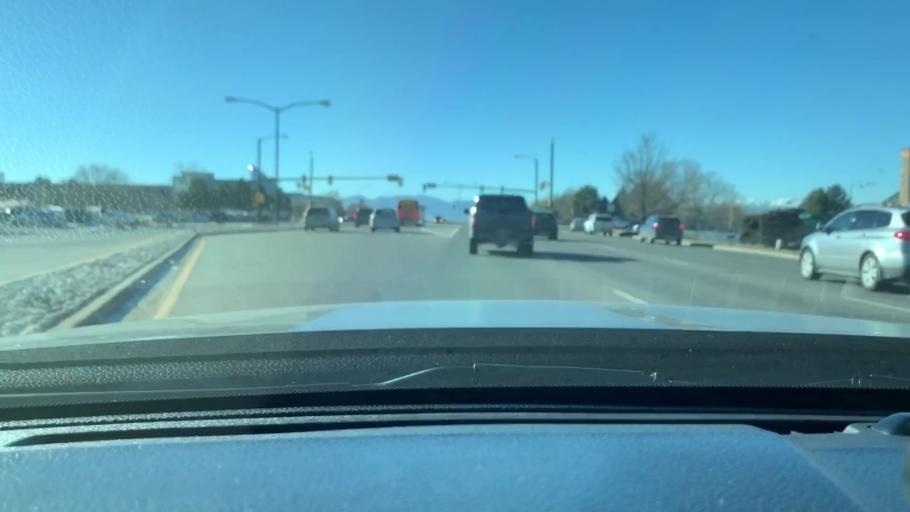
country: US
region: Colorado
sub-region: Adams County
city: Northglenn
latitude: 39.9141
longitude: -104.9954
